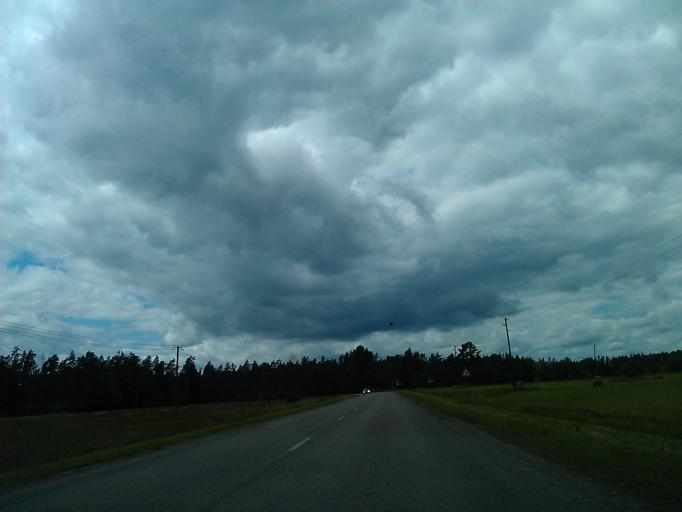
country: LV
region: Talsu Rajons
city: Stende
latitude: 57.0870
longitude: 22.3123
